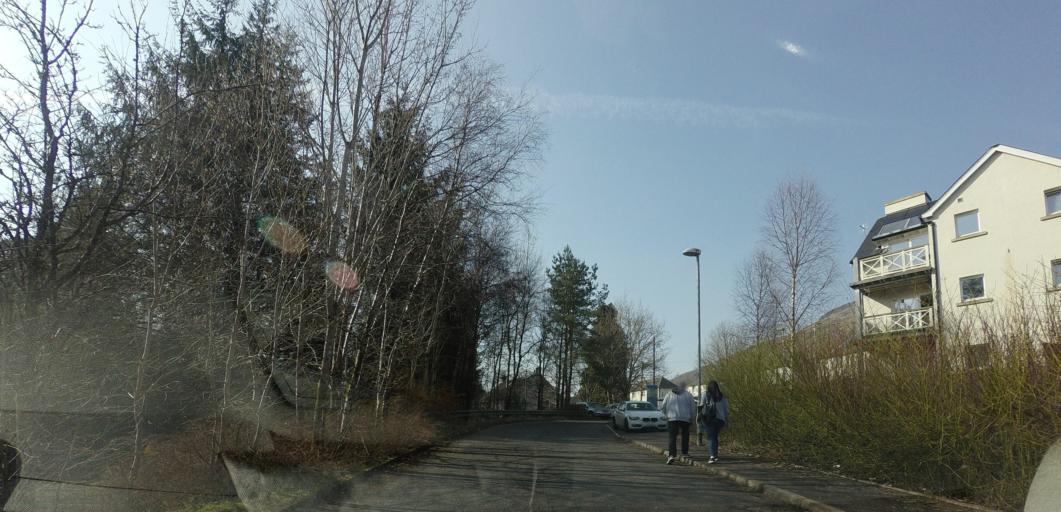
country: GB
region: Scotland
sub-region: Stirling
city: Callander
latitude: 56.4644
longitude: -4.3186
